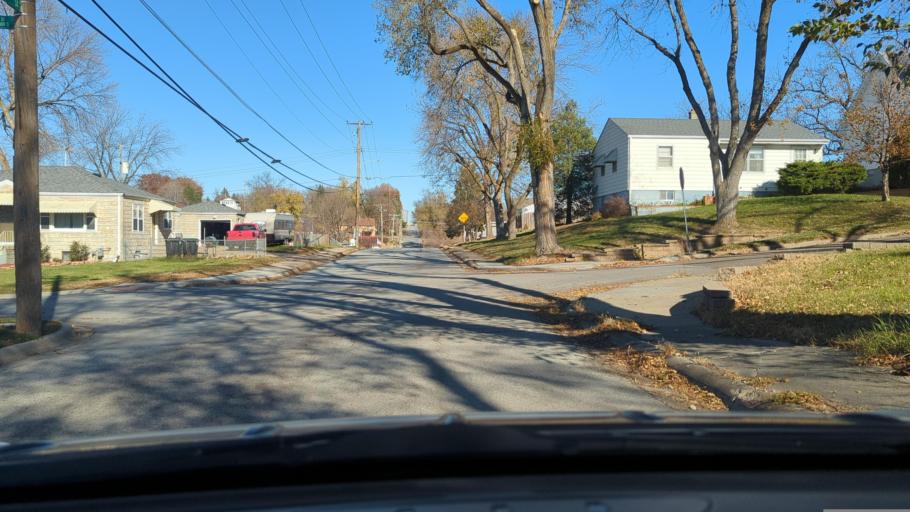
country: US
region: Nebraska
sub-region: Sarpy County
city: La Vista
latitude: 41.1915
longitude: -95.9770
